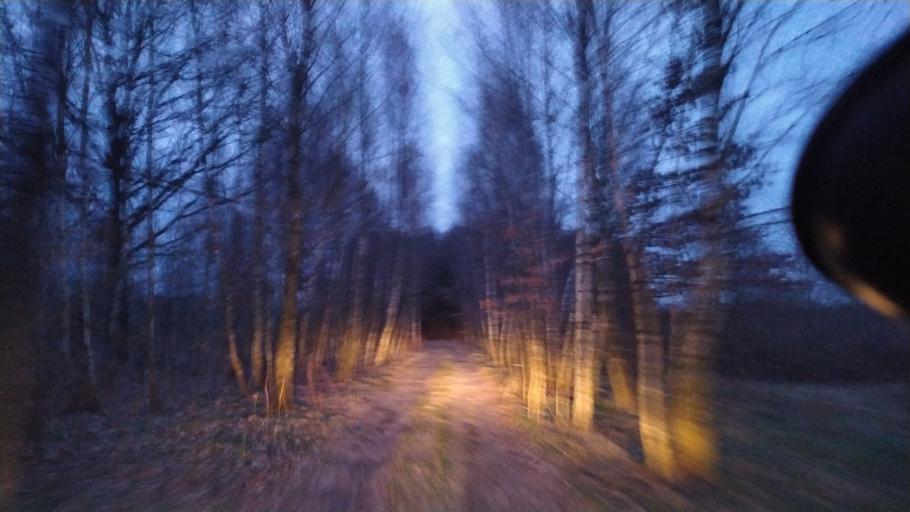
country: PL
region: Lublin Voivodeship
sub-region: Powiat lubelski
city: Jastkow
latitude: 51.3873
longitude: 22.4346
